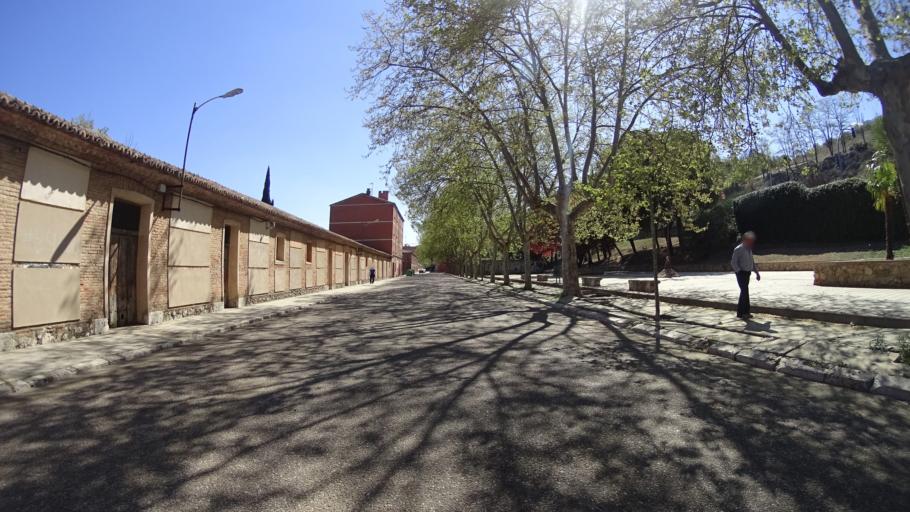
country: ES
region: Castille and Leon
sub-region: Provincia de Valladolid
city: Valladolid
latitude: 41.6647
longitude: -4.7393
